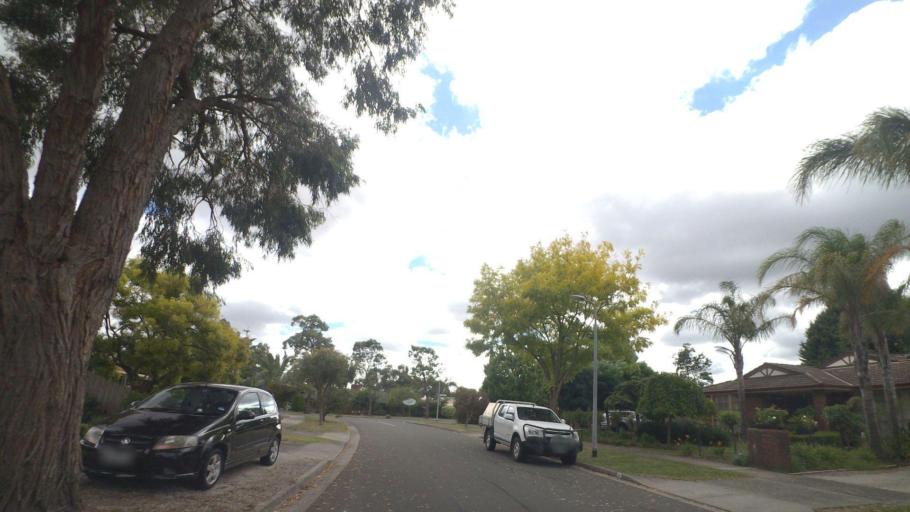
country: AU
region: Victoria
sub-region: Maroondah
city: Bayswater North
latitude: -37.8384
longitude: 145.3049
